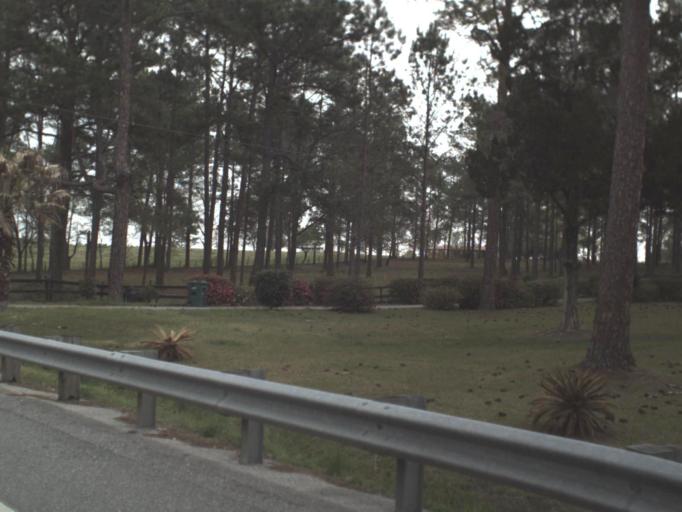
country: US
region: Florida
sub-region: Holmes County
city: Bonifay
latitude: 30.8196
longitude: -85.6703
